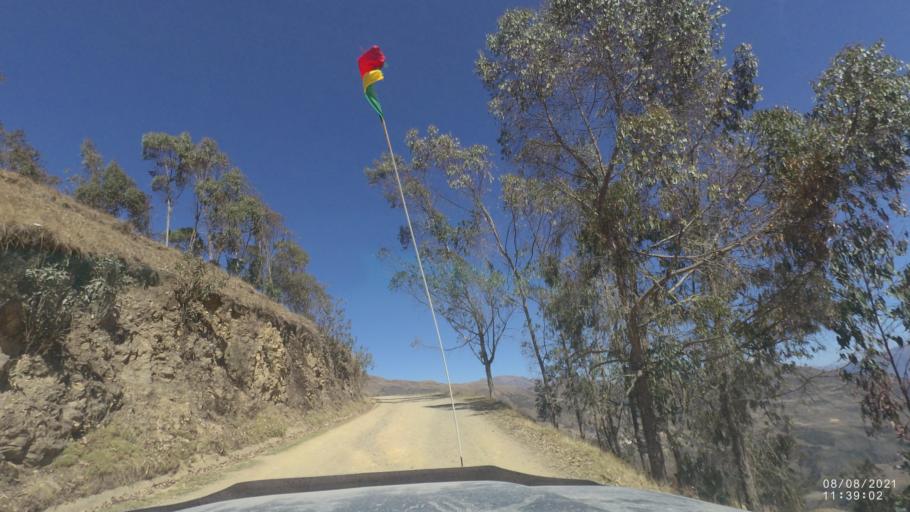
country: BO
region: Cochabamba
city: Colchani
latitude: -16.7925
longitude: -66.6509
